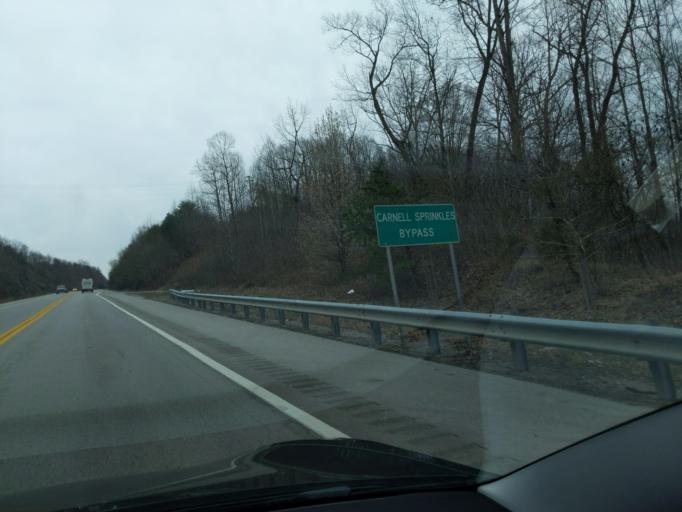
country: US
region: Kentucky
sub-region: Whitley County
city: Corbin
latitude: 36.9161
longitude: -84.0828
